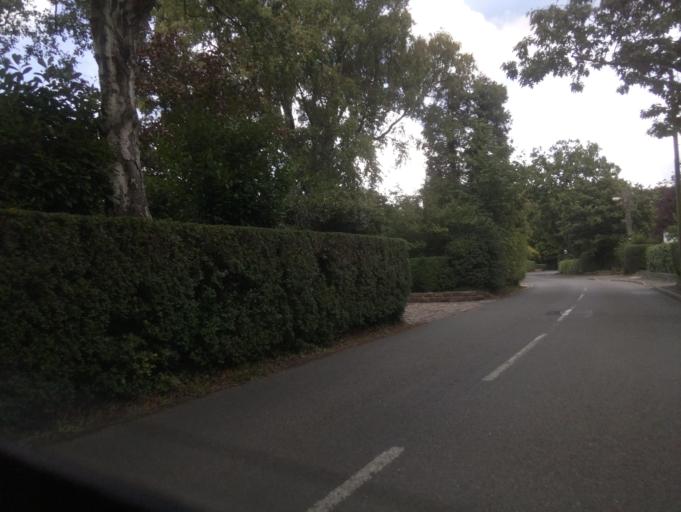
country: GB
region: England
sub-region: Staffordshire
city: Barlaston
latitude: 52.9405
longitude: -2.1745
